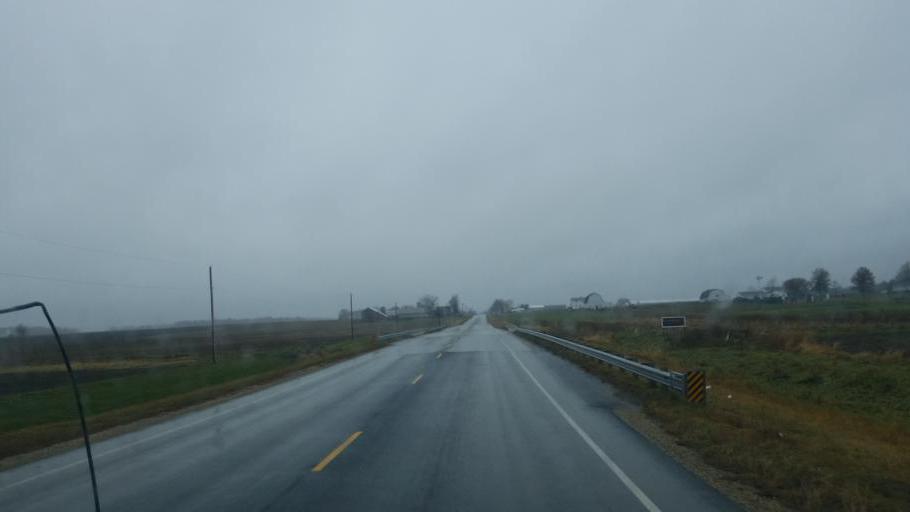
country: US
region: Indiana
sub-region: Adams County
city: Berne
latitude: 40.6585
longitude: -84.9114
